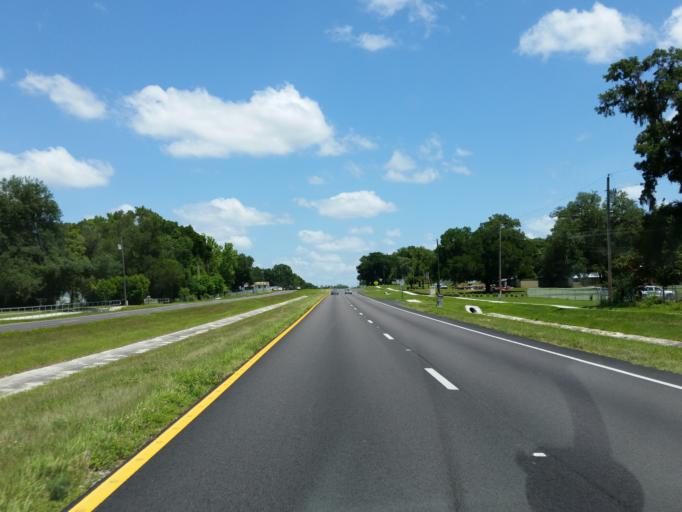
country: US
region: Florida
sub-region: Pasco County
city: Lacoochee
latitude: 28.4311
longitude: -82.1911
